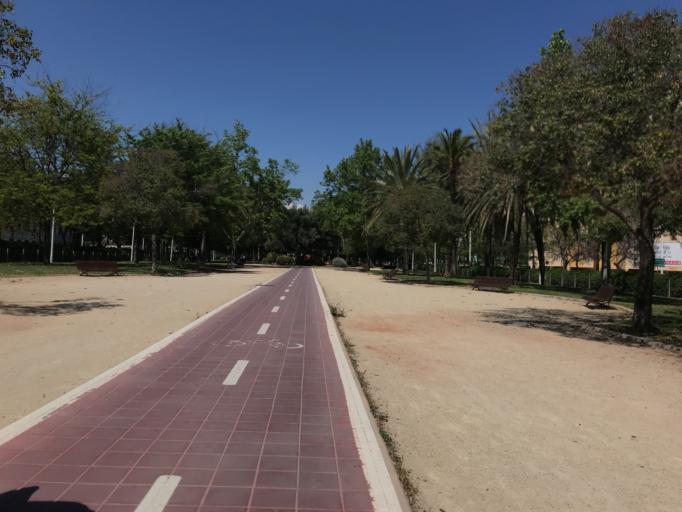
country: ES
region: Valencia
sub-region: Provincia de Valencia
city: Mislata
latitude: 39.4655
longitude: -0.4059
